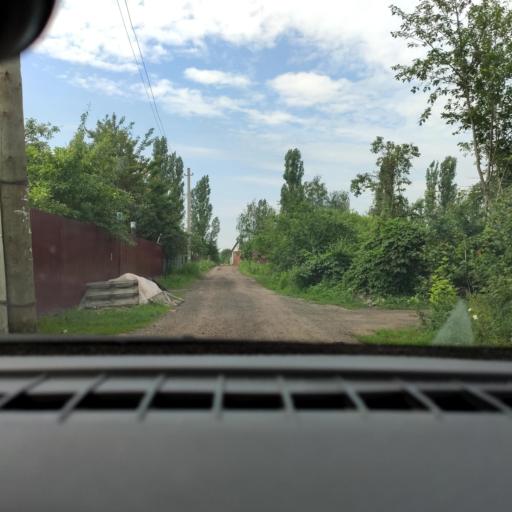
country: RU
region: Voronezj
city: Maslovka
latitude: 51.5020
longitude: 39.1986
